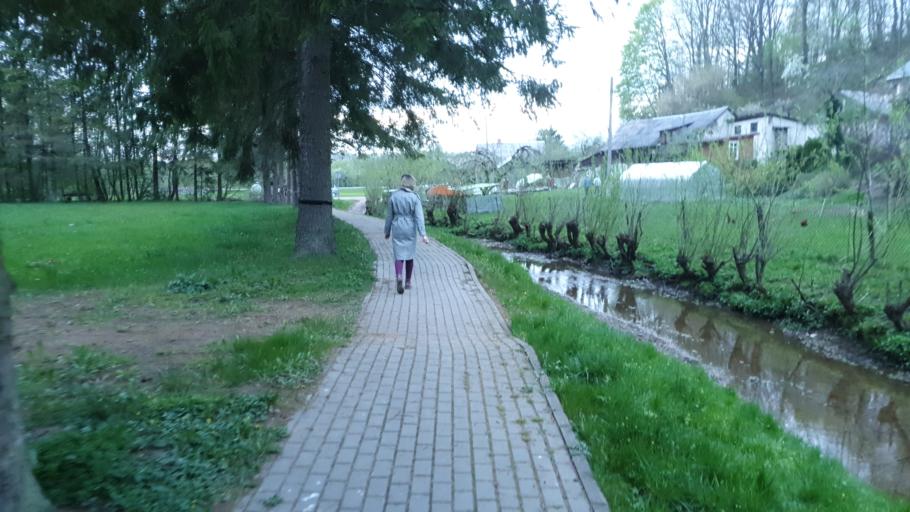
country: LT
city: Sakiai
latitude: 55.0819
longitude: 23.1779
